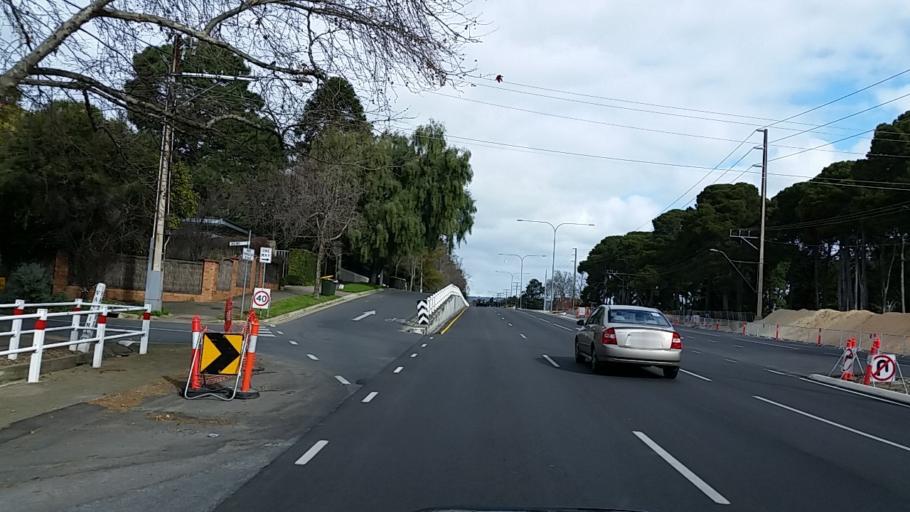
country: AU
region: South Australia
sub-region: Adelaide
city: Adelaide
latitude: -34.9128
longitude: 138.6136
